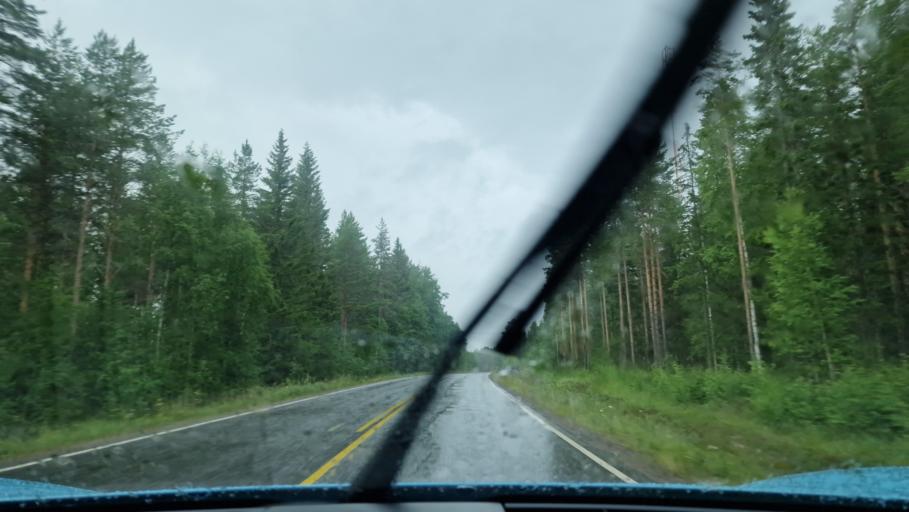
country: FI
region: Southern Ostrobothnia
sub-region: Jaerviseutu
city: Soini
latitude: 62.8189
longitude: 24.3501
